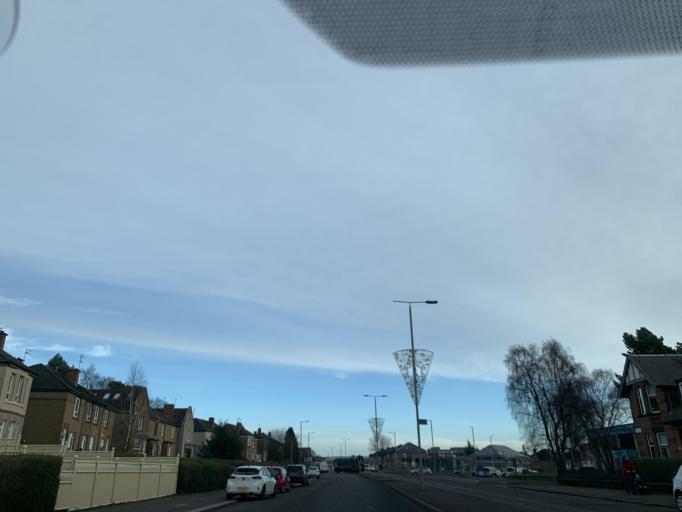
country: GB
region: Scotland
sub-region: Renfrewshire
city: Renfrew
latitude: 55.8458
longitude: -4.3498
